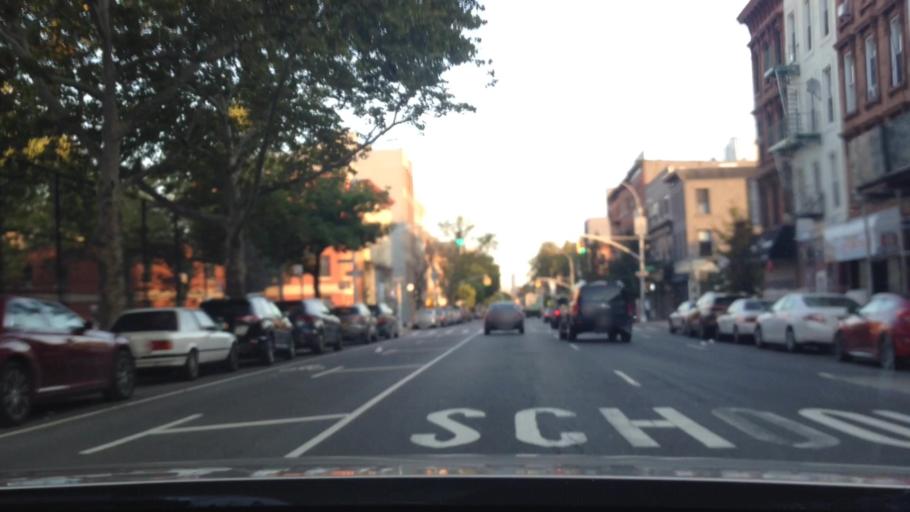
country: US
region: New York
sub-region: Kings County
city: Brooklyn
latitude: 40.6823
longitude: -73.9538
